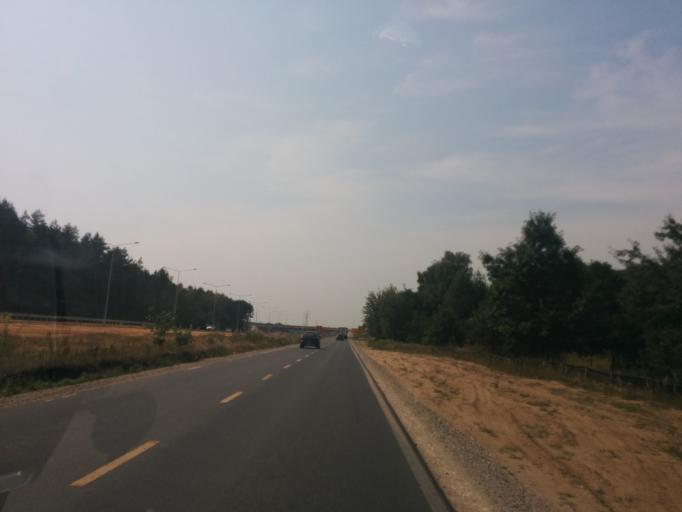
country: PL
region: Masovian Voivodeship
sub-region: Powiat pruszkowski
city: Nadarzyn
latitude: 52.1089
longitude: 20.8429
